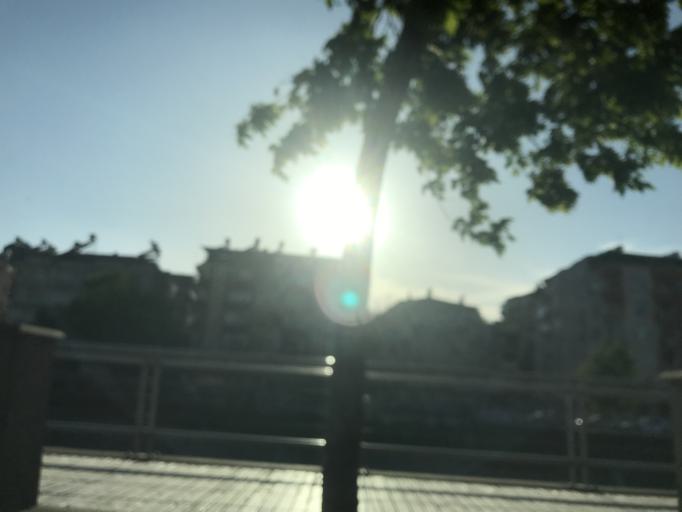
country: TR
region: Hatay
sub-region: Antakya Ilcesi
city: Antakya
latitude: 36.2049
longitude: 36.1621
